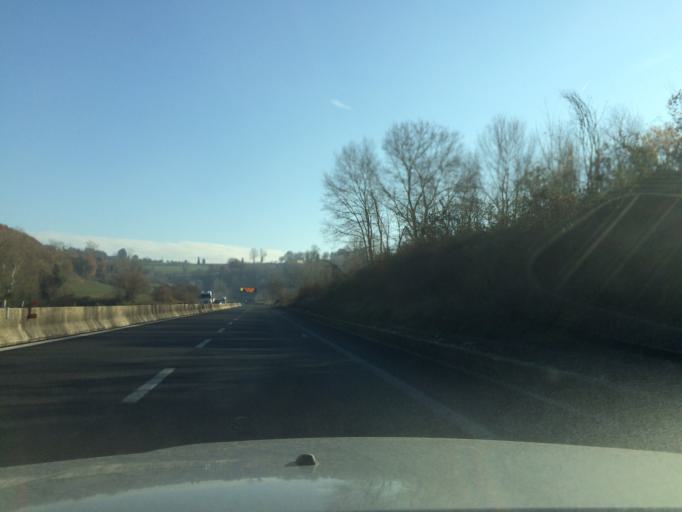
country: IT
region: Umbria
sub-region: Provincia di Perugia
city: Todi
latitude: 42.7514
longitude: 12.4660
